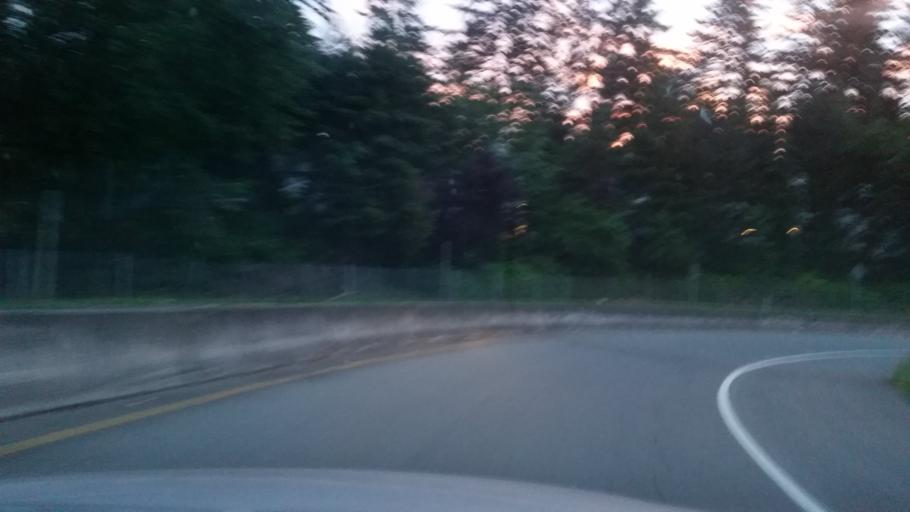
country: US
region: Washington
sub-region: Snohomish County
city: Esperance
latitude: 47.7787
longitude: -122.3469
